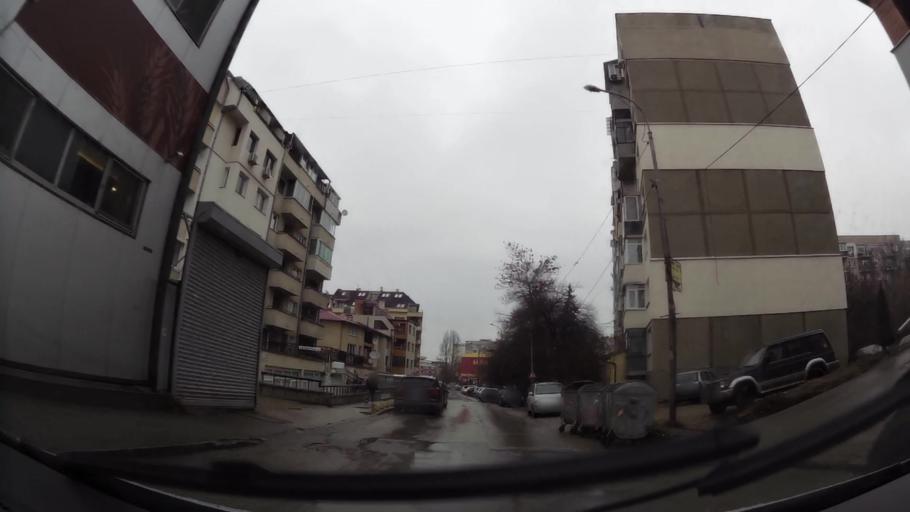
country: BG
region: Sofia-Capital
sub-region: Stolichna Obshtina
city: Sofia
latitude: 42.6416
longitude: 23.3665
